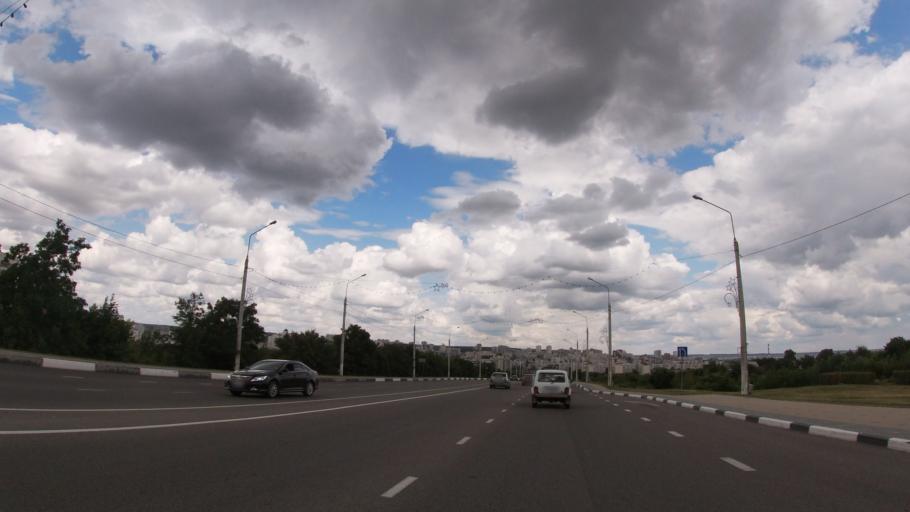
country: RU
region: Belgorod
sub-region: Belgorodskiy Rayon
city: Belgorod
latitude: 50.5814
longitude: 36.5834
